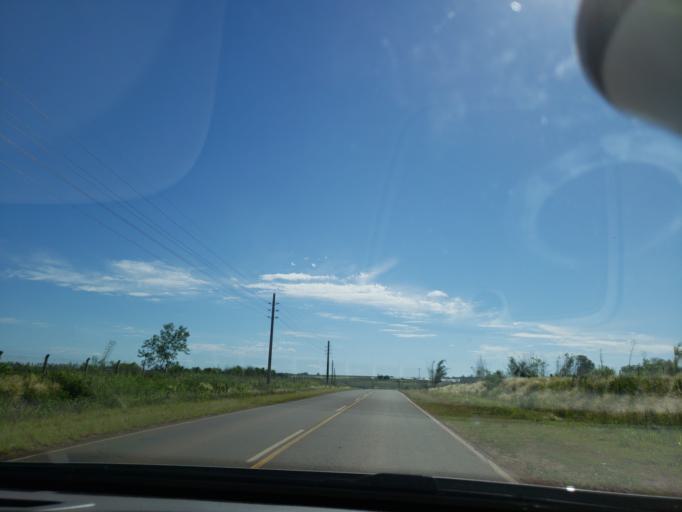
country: AR
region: Misiones
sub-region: Departamento de Capital
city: Posadas
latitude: -27.3876
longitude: -55.9775
